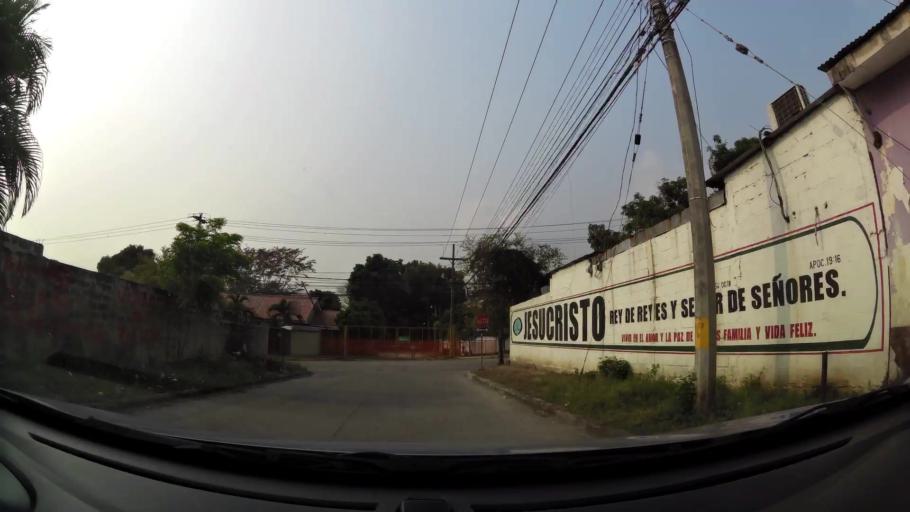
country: HN
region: Cortes
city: Armenta
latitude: 15.4835
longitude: -88.0381
